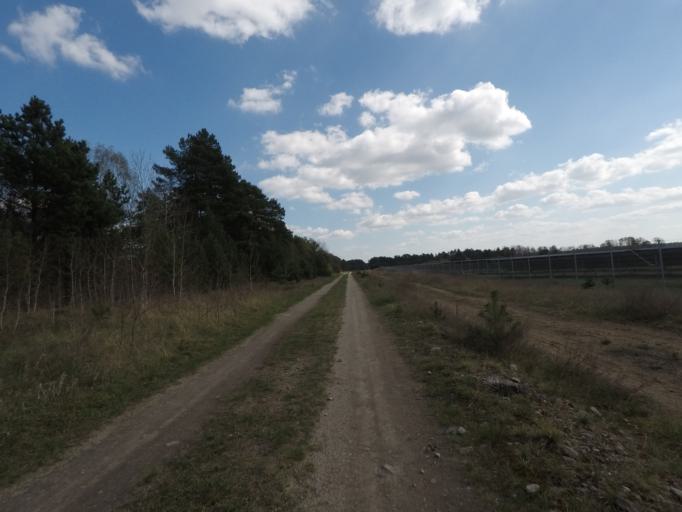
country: DE
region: Brandenburg
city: Melchow
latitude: 52.8340
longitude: 13.7068
